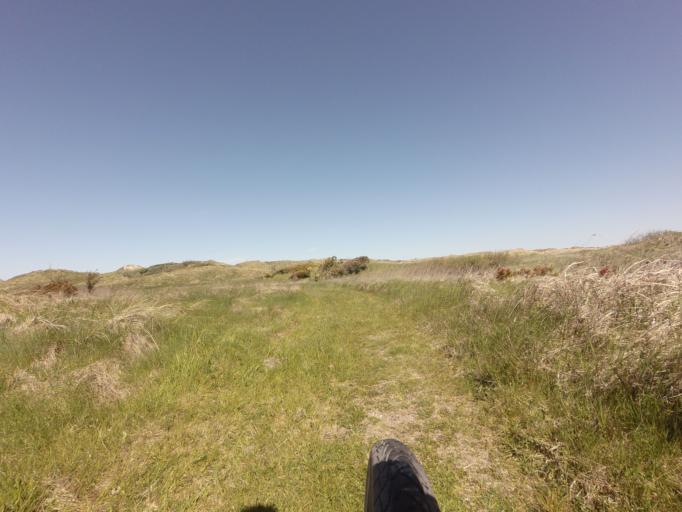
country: DK
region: North Denmark
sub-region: Jammerbugt Kommune
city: Pandrup
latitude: 57.2329
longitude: 9.5580
